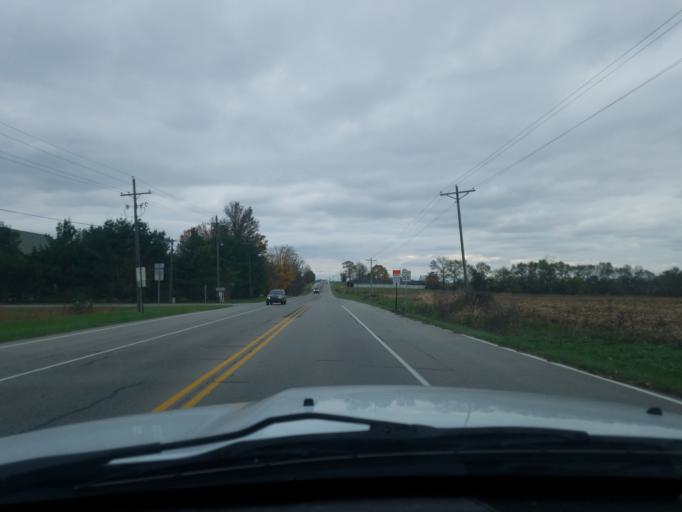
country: US
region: Indiana
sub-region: Bartholomew County
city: Hope
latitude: 39.2866
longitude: -85.7715
